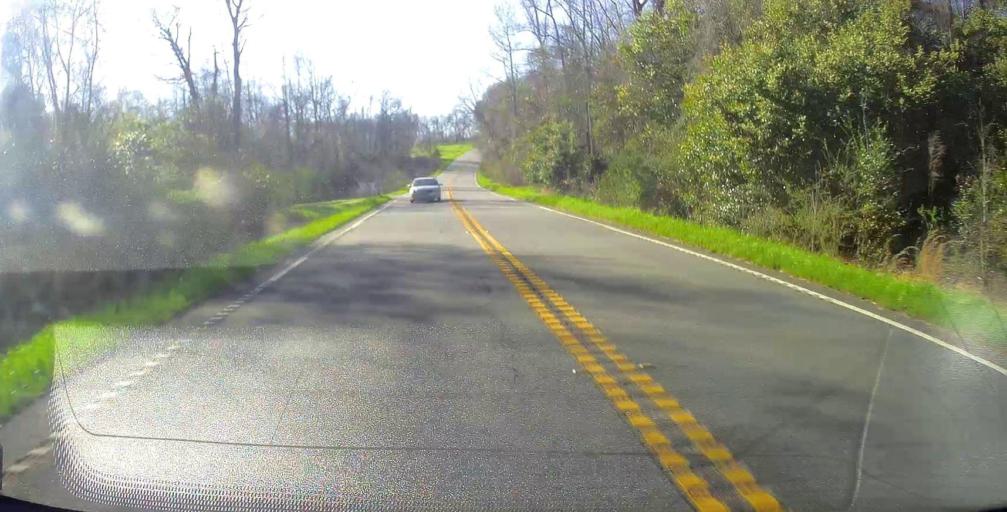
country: US
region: Georgia
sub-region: Macon County
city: Marshallville
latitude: 32.4402
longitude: -83.8866
